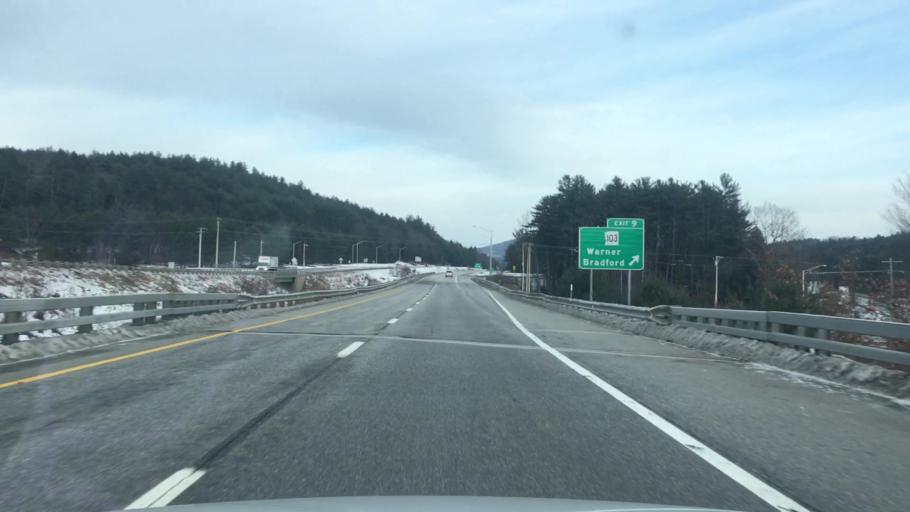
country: US
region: New Hampshire
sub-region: Merrimack County
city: Henniker
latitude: 43.2880
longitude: -71.8356
